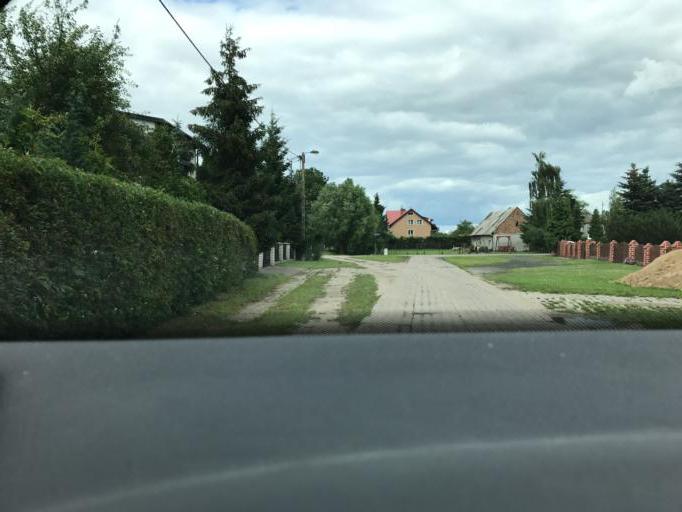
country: PL
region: Pomeranian Voivodeship
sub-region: Powiat gdanski
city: Pruszcz Gdanski
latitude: 54.2750
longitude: 18.6911
